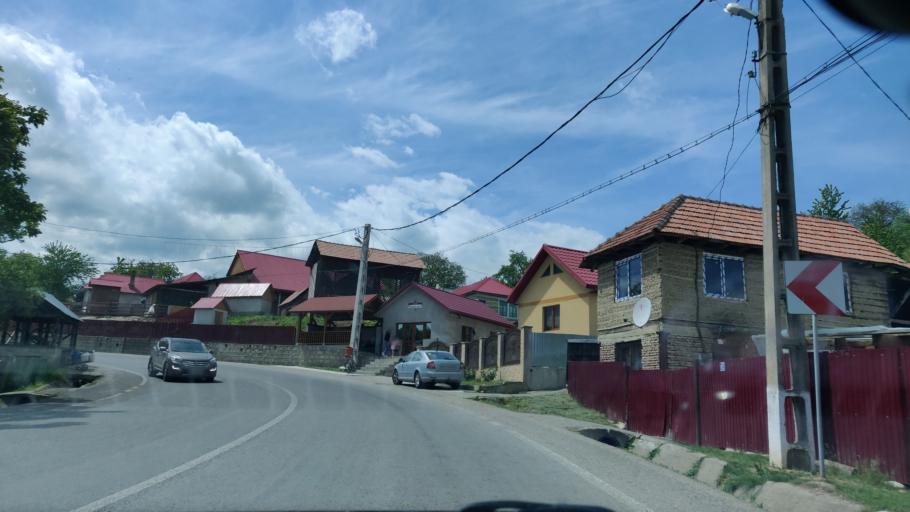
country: RO
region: Vrancea
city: Matacina
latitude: 45.8919
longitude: 26.8390
